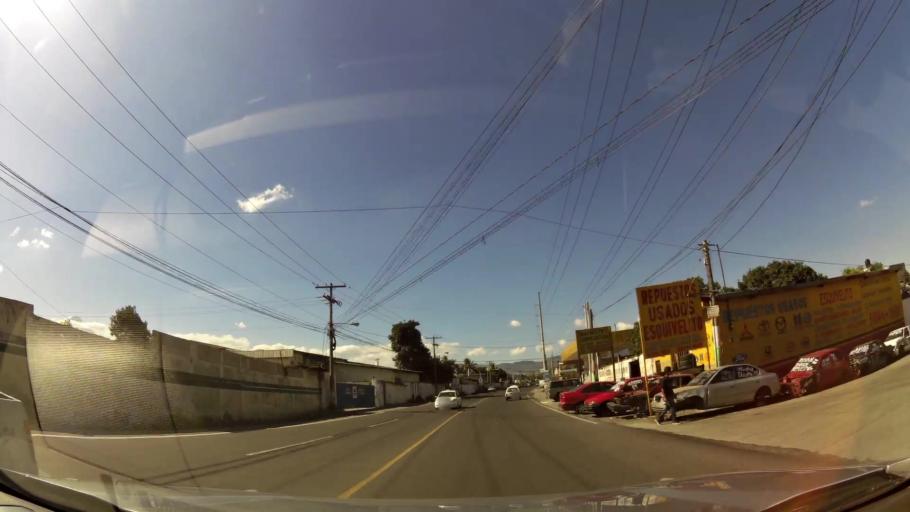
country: GT
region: Guatemala
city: Petapa
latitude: 14.5051
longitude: -90.5669
